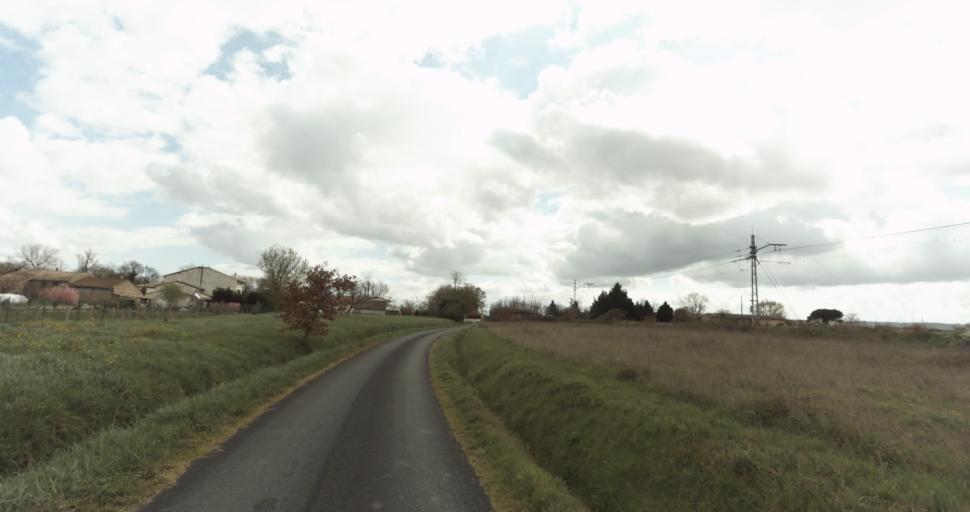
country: FR
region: Midi-Pyrenees
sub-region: Departement de la Haute-Garonne
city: Auterive
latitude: 43.3345
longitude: 1.4823
